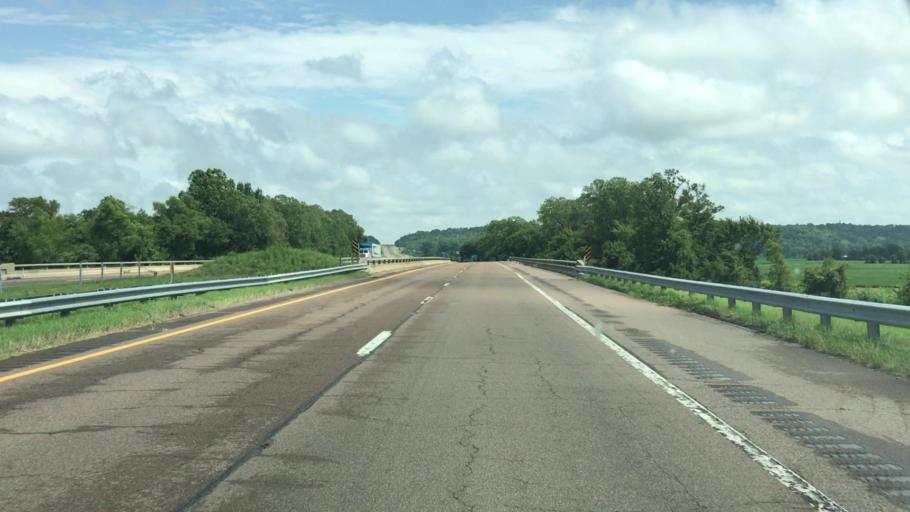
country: US
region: Tennessee
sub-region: Dyer County
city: Dyersburg
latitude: 36.0784
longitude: -89.5191
